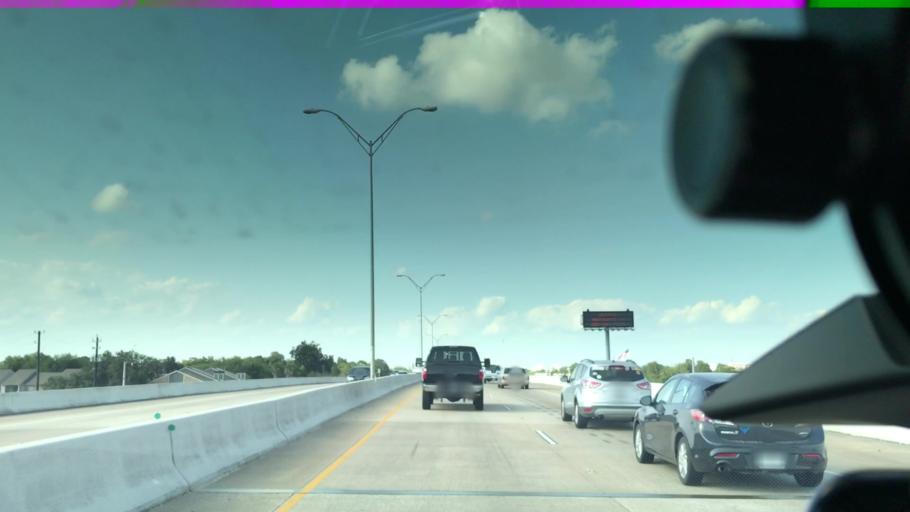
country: US
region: Texas
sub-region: Harris County
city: Deer Park
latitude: 29.7010
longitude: -95.1535
